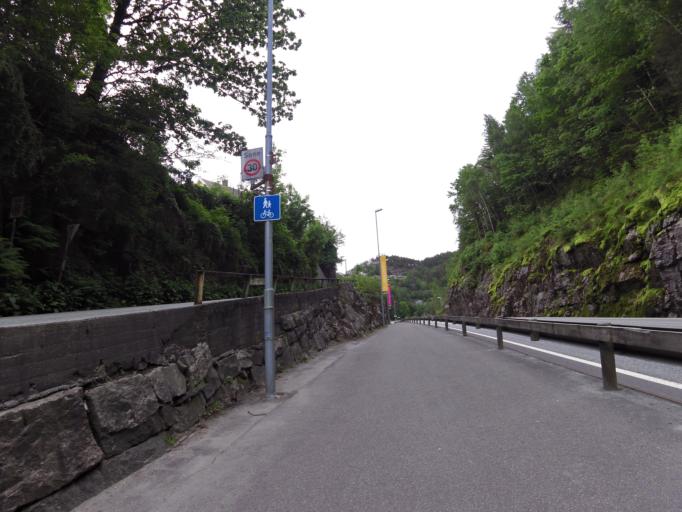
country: NO
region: Vest-Agder
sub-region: Flekkefjord
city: Flekkefjord
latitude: 58.2977
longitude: 6.6737
